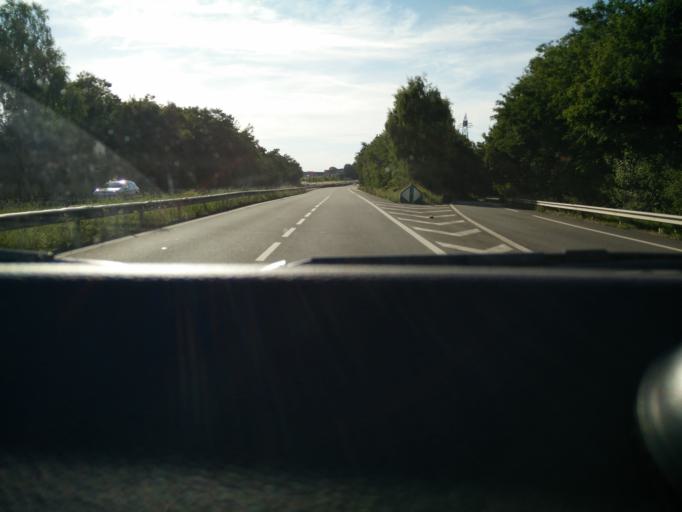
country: FR
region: Nord-Pas-de-Calais
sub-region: Departement du Nord
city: Escaudain
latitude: 50.3240
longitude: 3.3465
